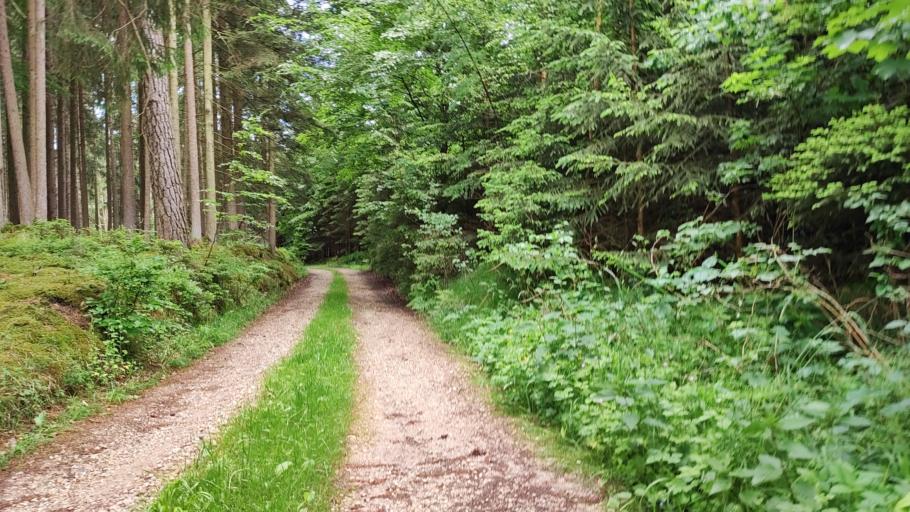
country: DE
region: Bavaria
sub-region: Swabia
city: Landensberg
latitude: 48.4344
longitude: 10.5435
